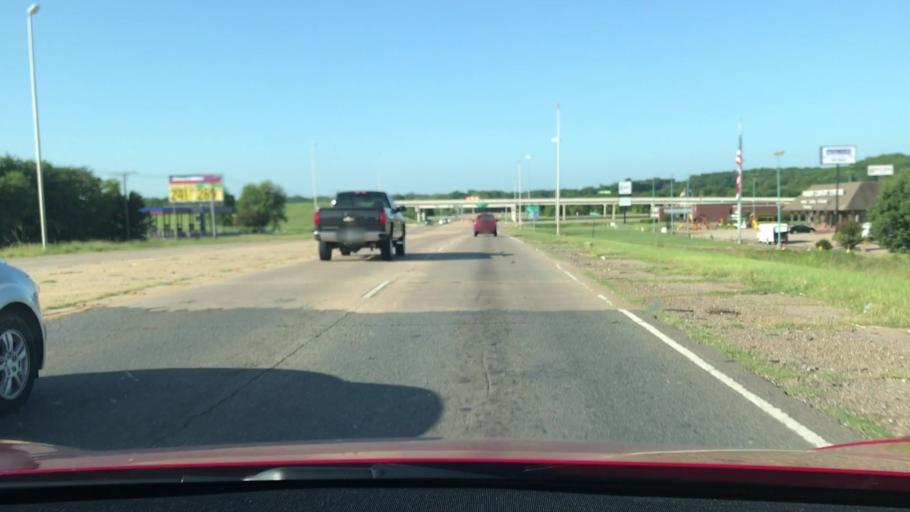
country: US
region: Louisiana
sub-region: Bossier Parish
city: Bossier City
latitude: 32.4148
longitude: -93.7236
